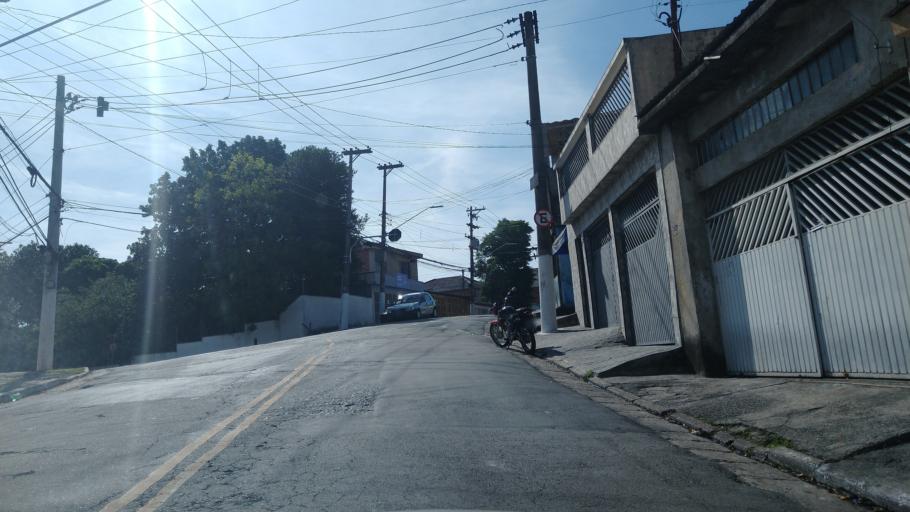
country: BR
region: Sao Paulo
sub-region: Sao Paulo
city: Sao Paulo
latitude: -23.4637
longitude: -46.6786
